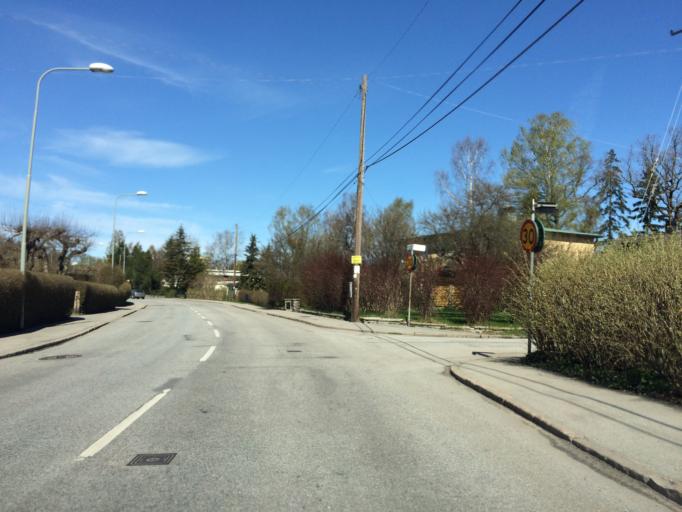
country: SE
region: Stockholm
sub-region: Huddinge Kommun
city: Segeltorp
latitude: 59.2784
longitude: 17.9620
